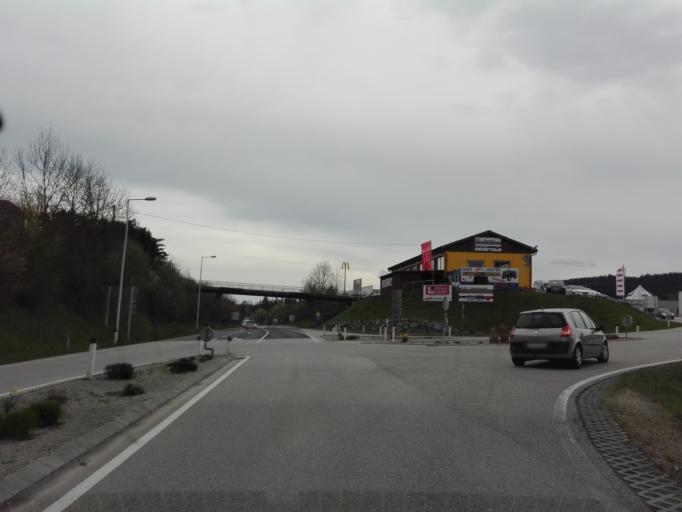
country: AT
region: Upper Austria
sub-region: Politischer Bezirk Rohrbach
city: Schlaegl
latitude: 48.5689
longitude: 13.9819
